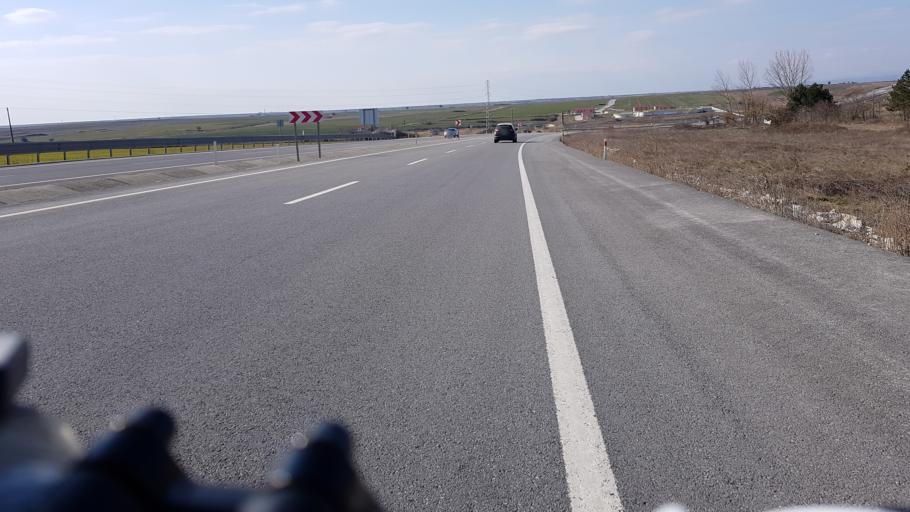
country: TR
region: Tekirdag
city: Saray
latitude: 41.4214
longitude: 27.9169
